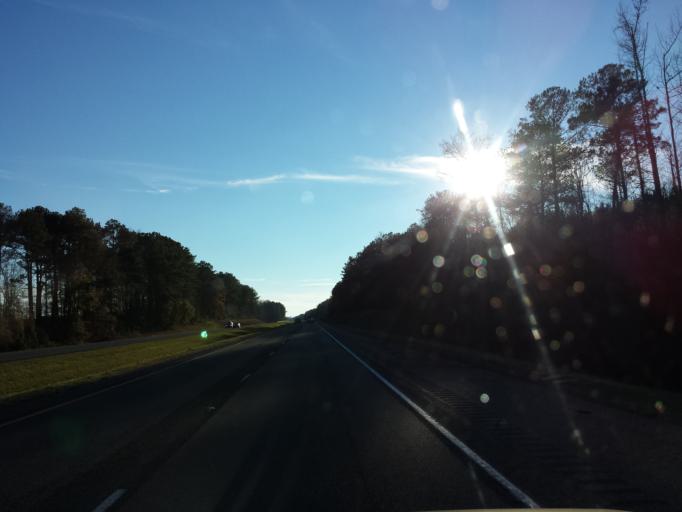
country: US
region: Alabama
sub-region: Greene County
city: Eutaw
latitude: 32.9343
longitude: -87.8560
